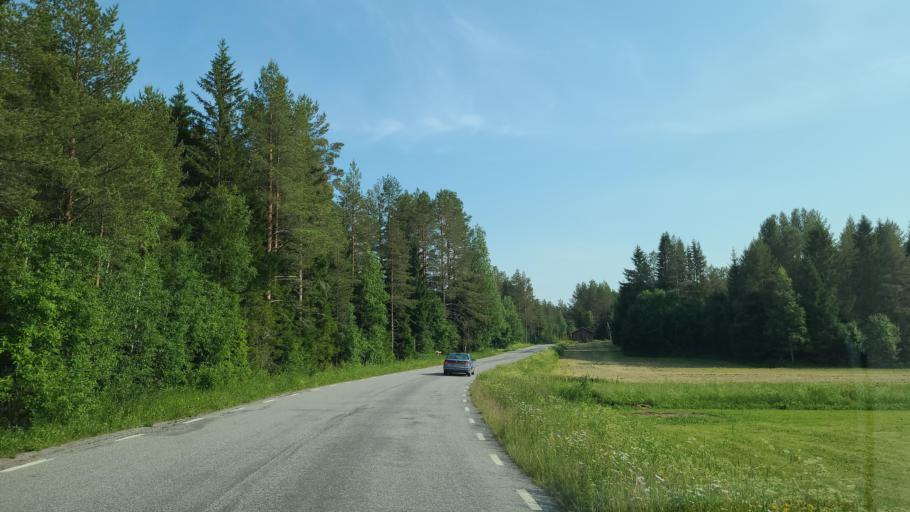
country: SE
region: Vaesterbotten
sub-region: Skelleftea Kommun
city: Burea
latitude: 64.3579
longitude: 21.3375
